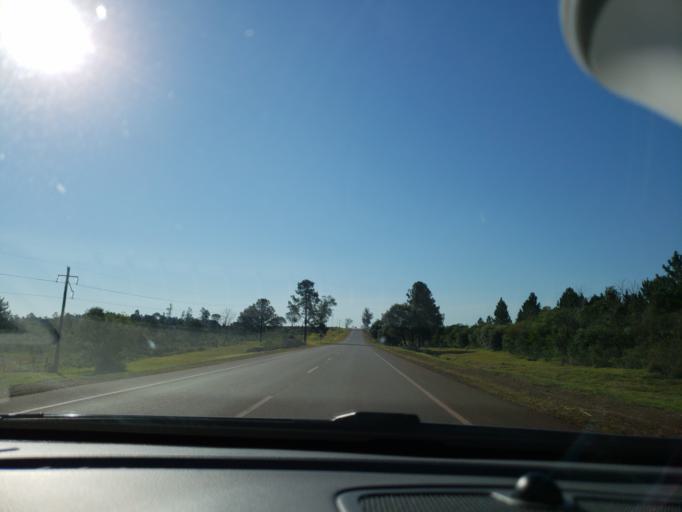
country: AR
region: Misiones
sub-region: Departamento de Apostoles
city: San Jose
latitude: -27.7933
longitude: -55.7713
